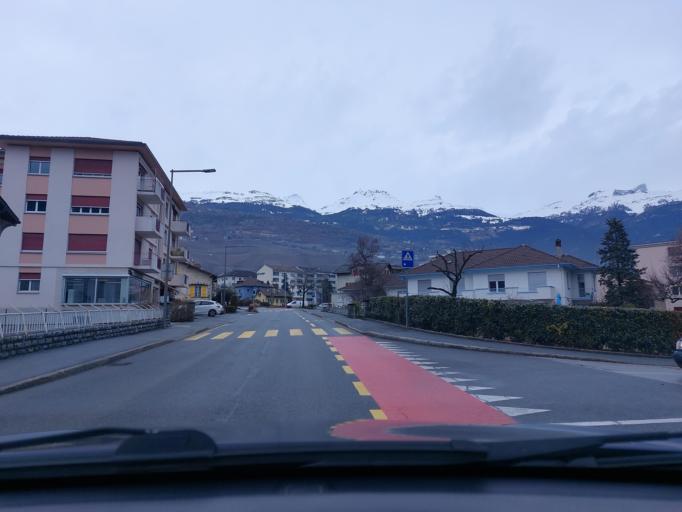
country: CH
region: Valais
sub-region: Sierre District
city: Sierre
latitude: 46.2875
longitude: 7.5254
